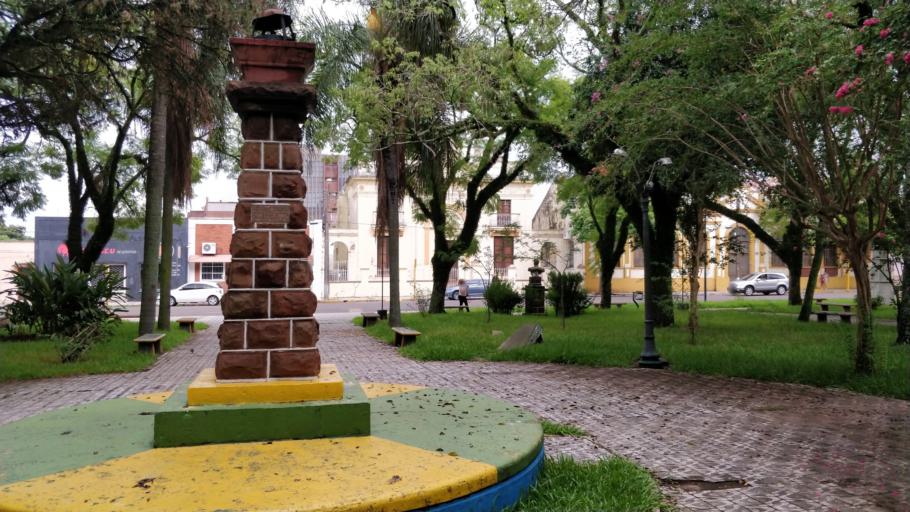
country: BR
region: Rio Grande do Sul
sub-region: Itaqui
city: Itaqui
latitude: -29.1220
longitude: -56.5566
